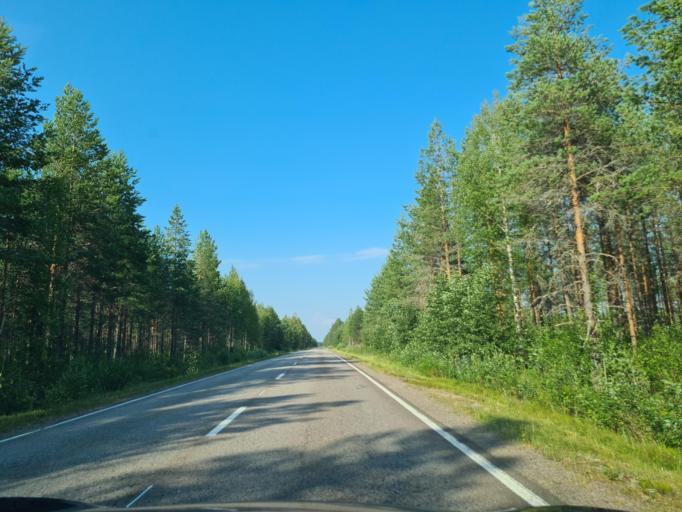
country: FI
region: Satakunta
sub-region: Pohjois-Satakunta
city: Karvia
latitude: 62.3011
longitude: 22.6349
